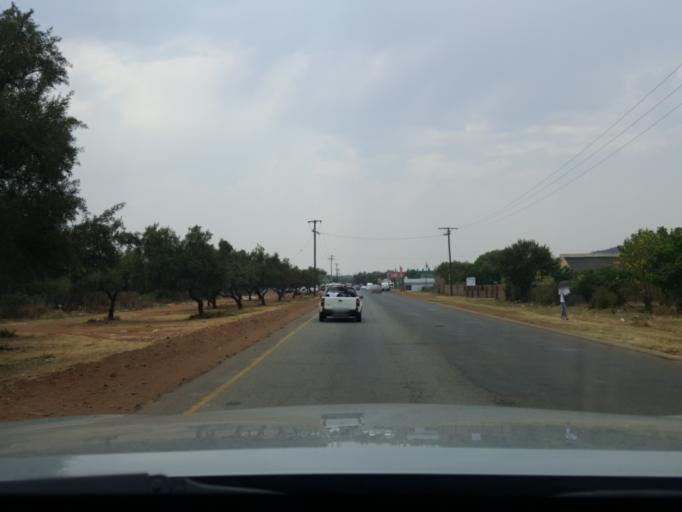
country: ZA
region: North-West
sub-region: Ngaka Modiri Molema District Municipality
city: Zeerust
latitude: -25.4963
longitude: 25.9841
